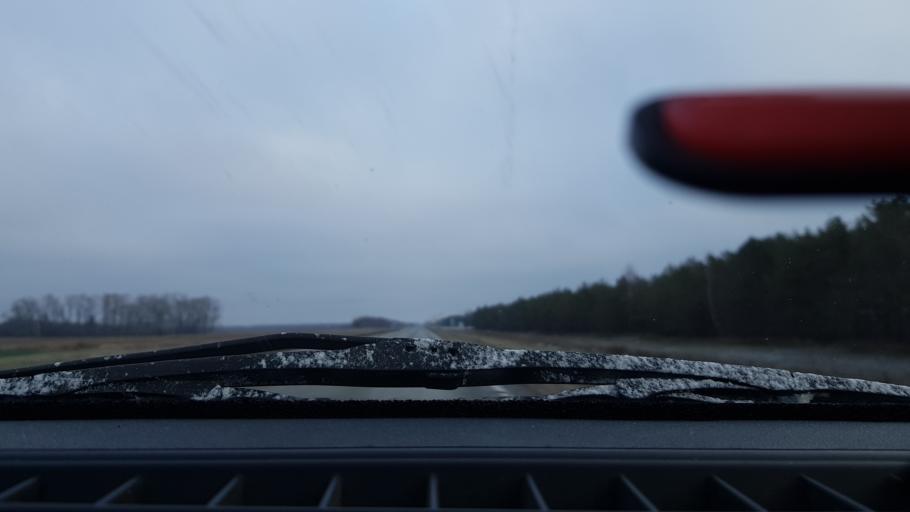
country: RU
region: Tatarstan
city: Kuybyshevskiy Zaton
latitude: 54.9520
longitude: 49.4666
